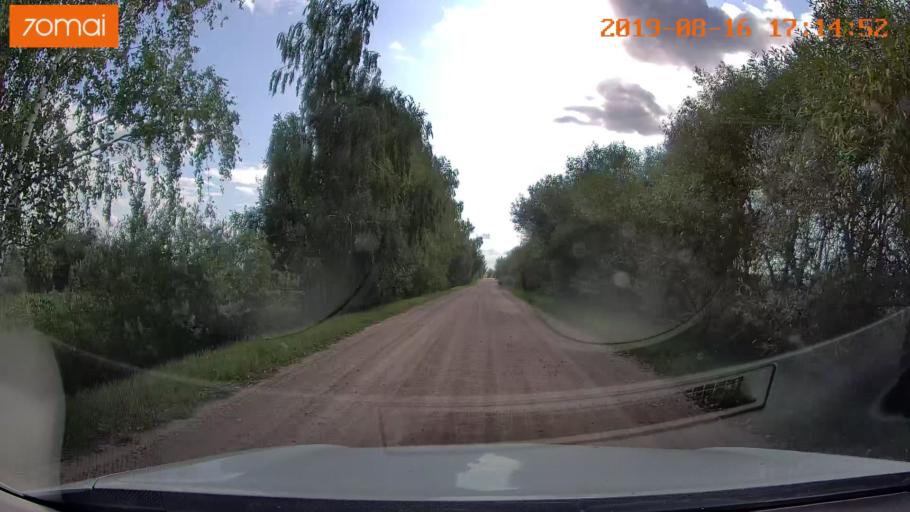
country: BY
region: Mogilev
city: Hlusha
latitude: 53.1819
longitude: 28.8518
